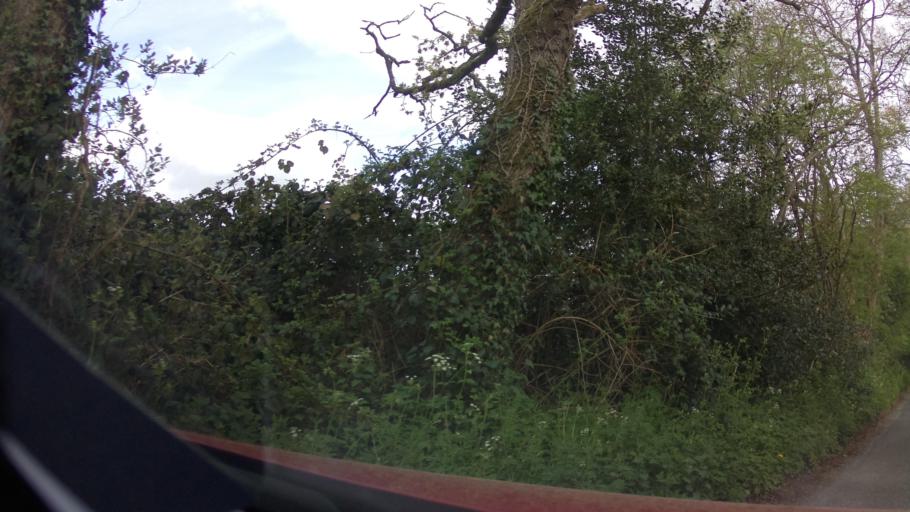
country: GB
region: England
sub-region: Hampshire
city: Romsey
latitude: 51.0246
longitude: -1.4841
